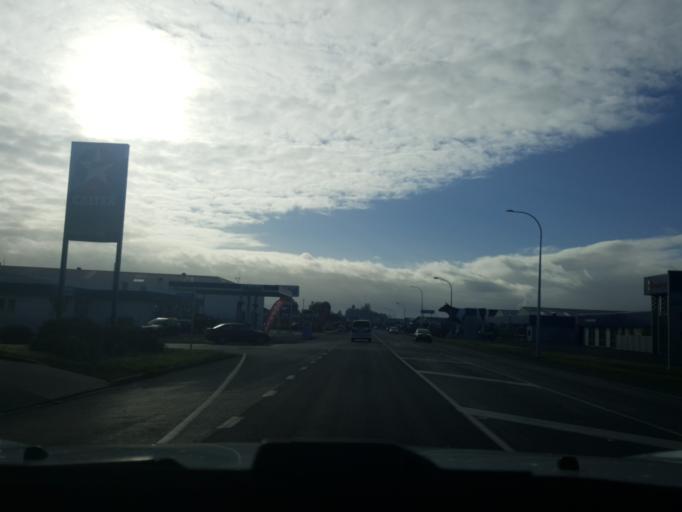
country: NZ
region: Waikato
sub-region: Waipa District
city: Cambridge
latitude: -37.6607
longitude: 175.5205
